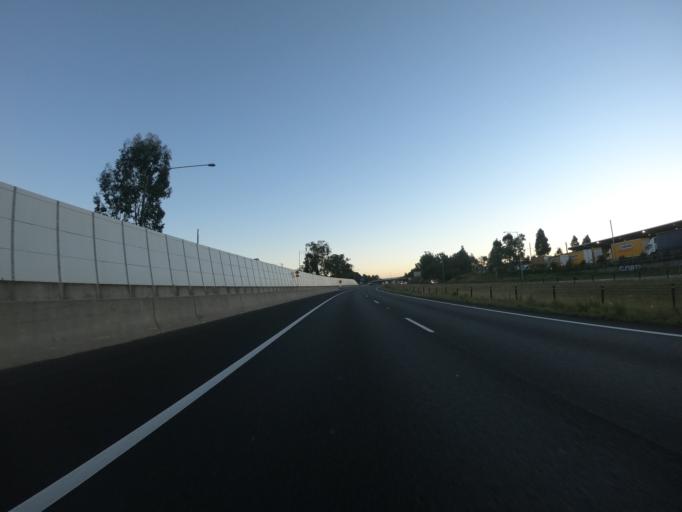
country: AU
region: New South Wales
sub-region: Blacktown
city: Glendenning
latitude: -33.7497
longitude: 150.8456
